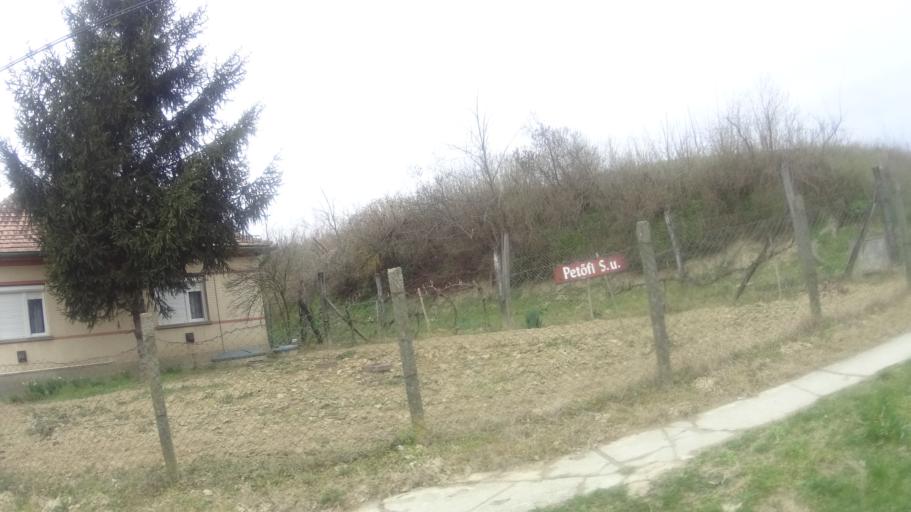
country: HU
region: Somogy
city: Adand
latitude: 46.8009
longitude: 18.1042
